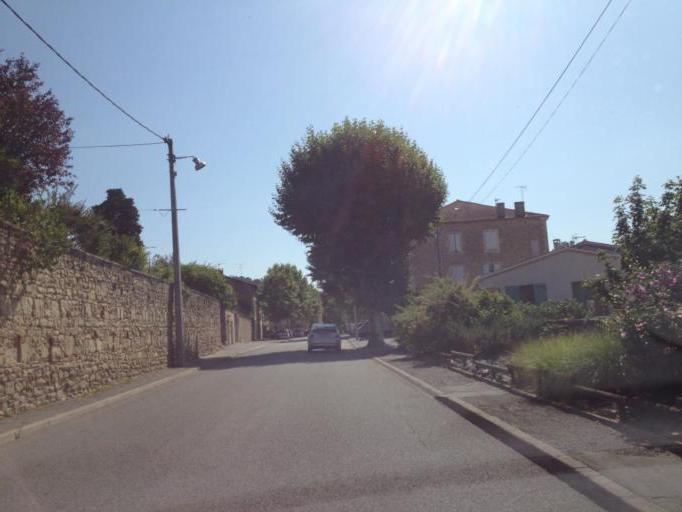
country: FR
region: Rhone-Alpes
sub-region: Departement de la Drome
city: Clerieux
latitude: 45.1213
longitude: 4.9776
